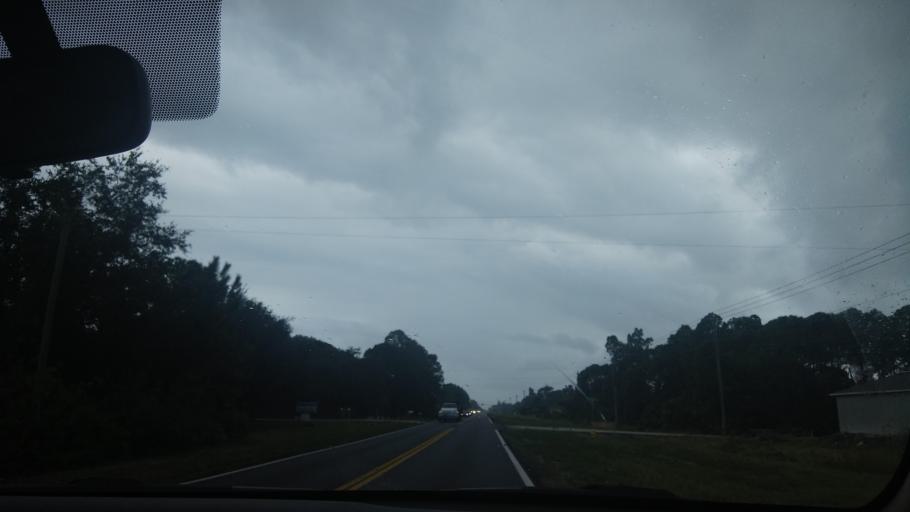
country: US
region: Florida
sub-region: Brevard County
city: Grant-Valkaria
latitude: 27.9591
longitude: -80.6226
